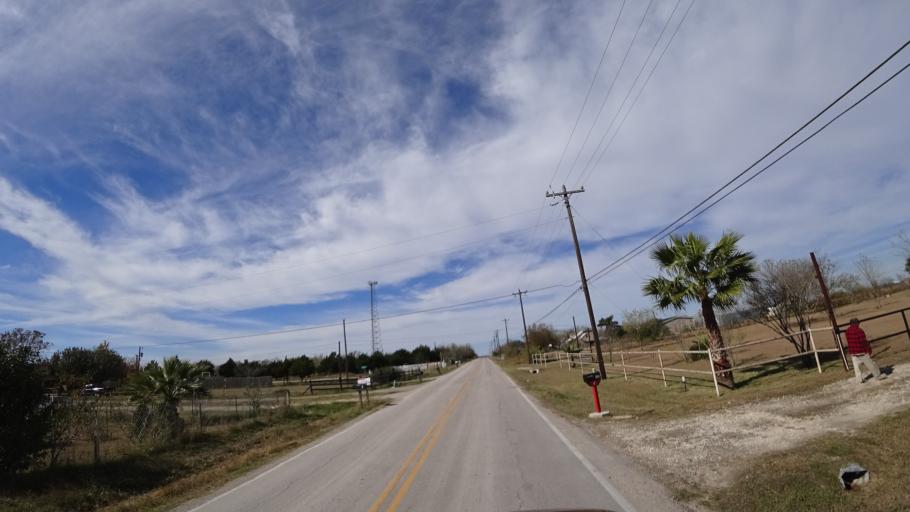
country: US
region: Texas
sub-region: Travis County
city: Onion Creek
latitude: 30.1143
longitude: -97.7012
